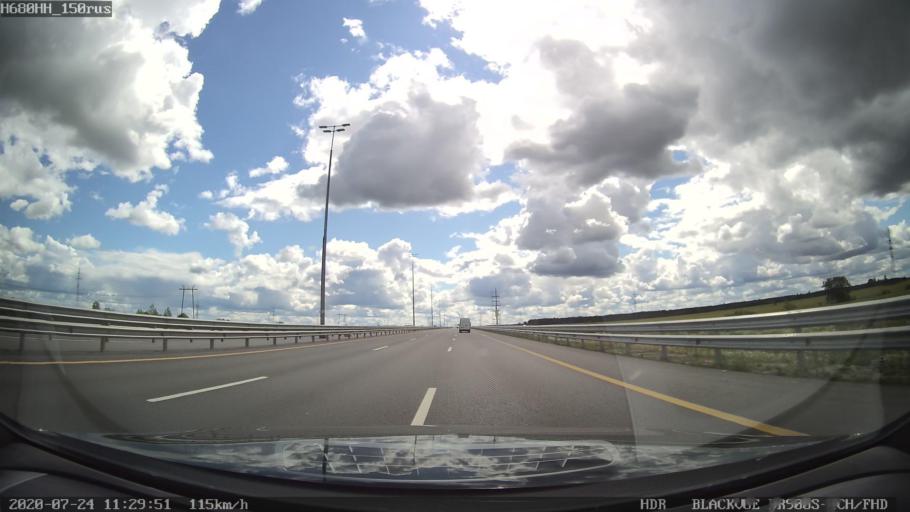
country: RU
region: Leningrad
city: Krasnyy Bor
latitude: 59.6761
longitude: 30.6003
